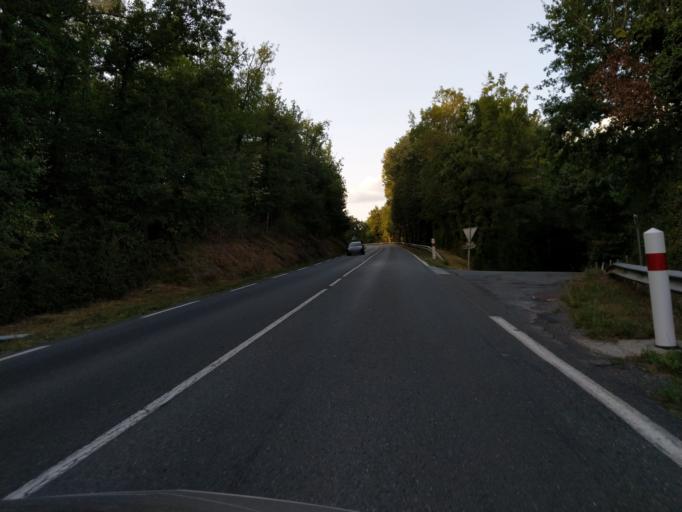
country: FR
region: Midi-Pyrenees
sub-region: Departement du Tarn
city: Realmont
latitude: 43.7917
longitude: 2.1882
